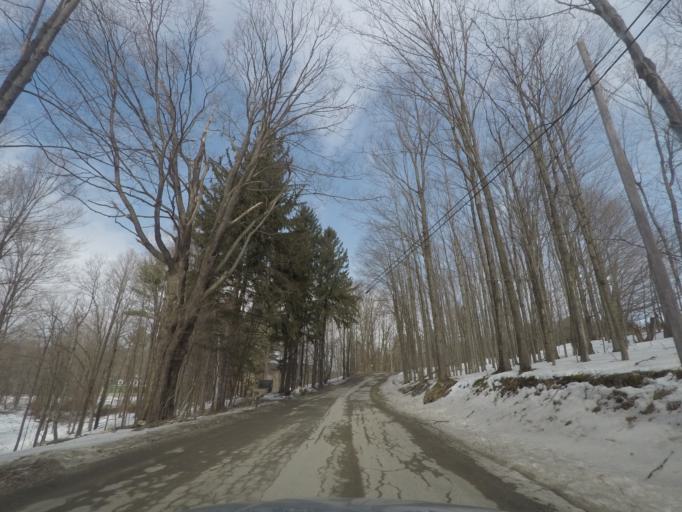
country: US
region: New York
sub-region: Saratoga County
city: Waterford
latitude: 42.7754
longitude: -73.6044
